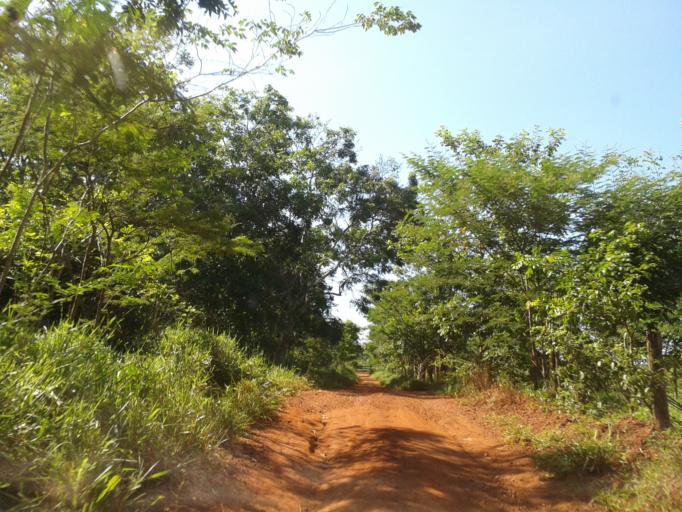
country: BR
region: Minas Gerais
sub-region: Santa Vitoria
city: Santa Vitoria
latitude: -19.1207
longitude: -50.5388
